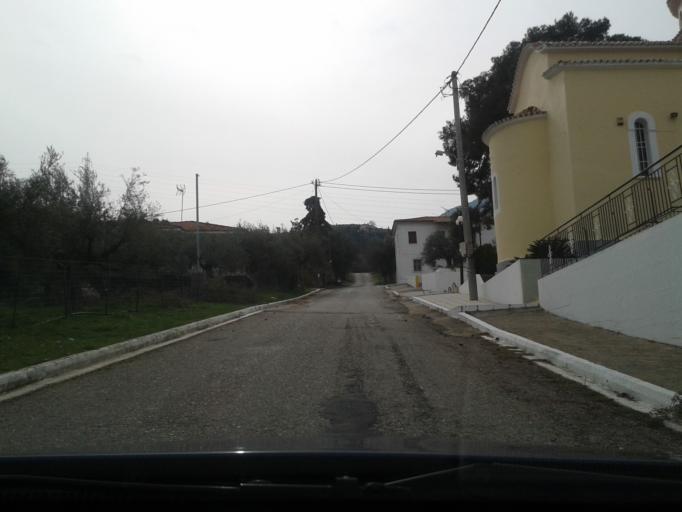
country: GR
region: West Greece
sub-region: Nomos Achaias
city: Akrata
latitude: 38.1747
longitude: 22.2299
